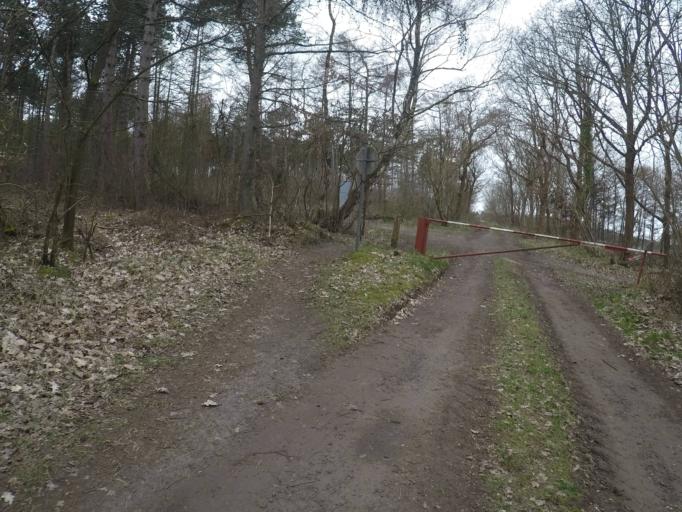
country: DE
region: Lower Saxony
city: Nordholz
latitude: 53.8270
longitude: 8.6001
